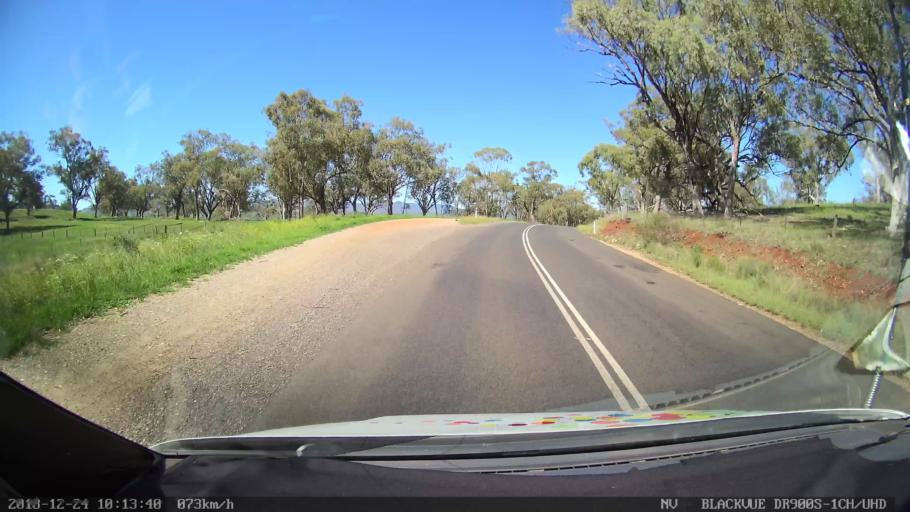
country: AU
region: New South Wales
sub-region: Liverpool Plains
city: Quirindi
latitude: -31.6922
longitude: 150.6378
